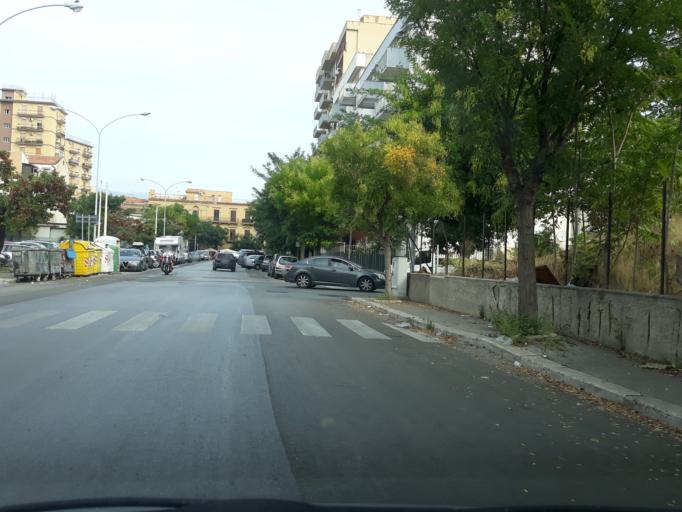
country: IT
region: Sicily
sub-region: Palermo
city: Palermo
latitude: 38.0992
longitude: 13.3252
